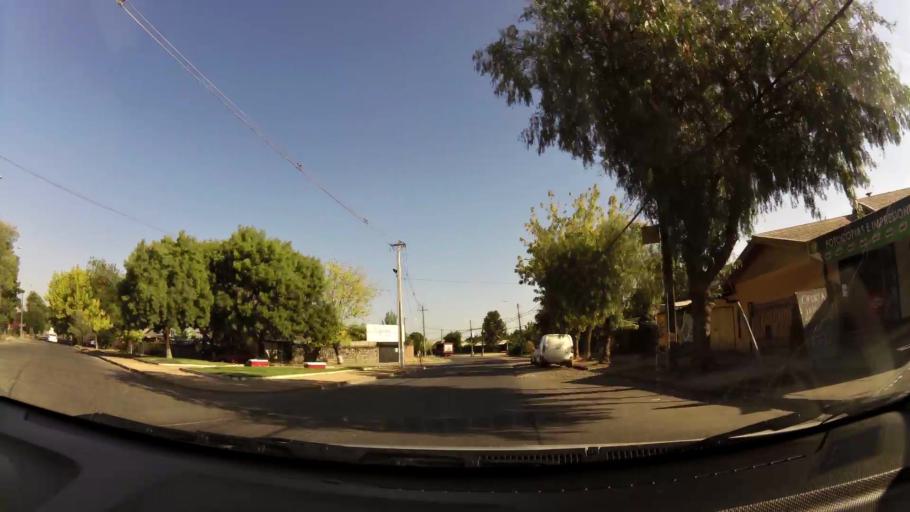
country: CL
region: Maule
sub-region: Provincia de Talca
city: Talca
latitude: -35.4403
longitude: -71.6700
